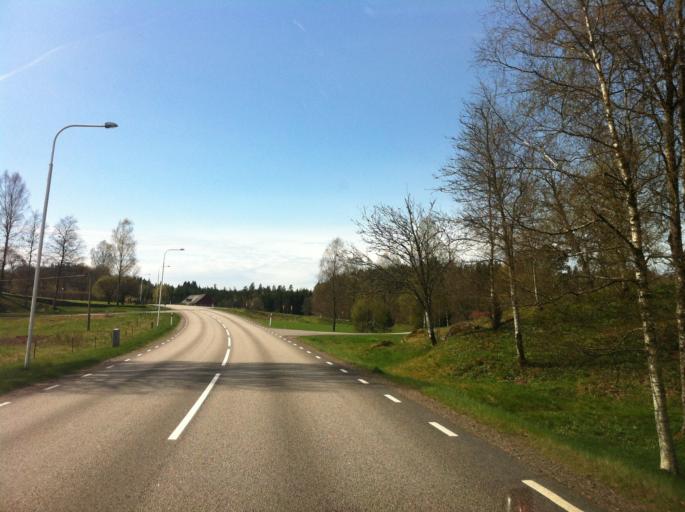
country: SE
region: Vaestra Goetaland
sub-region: Marks Kommun
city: Fritsla
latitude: 57.3115
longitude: 12.8826
